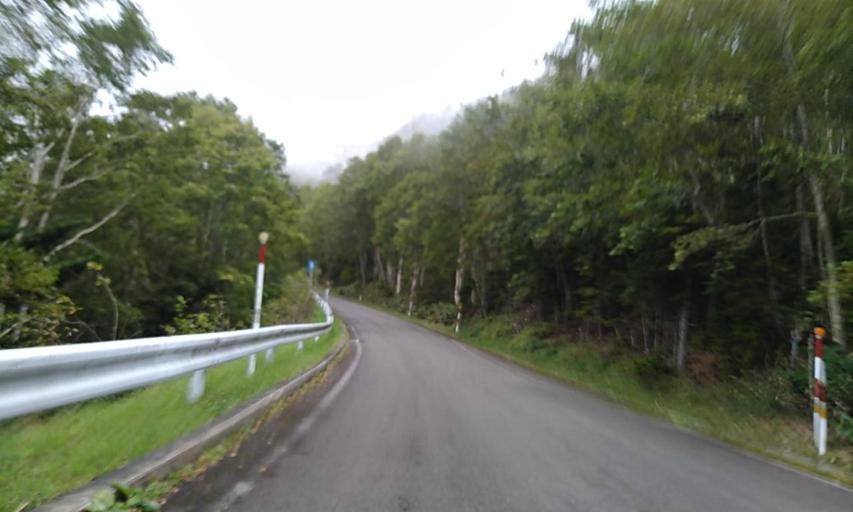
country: JP
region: Hokkaido
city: Bihoro
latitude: 43.5739
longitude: 144.2366
